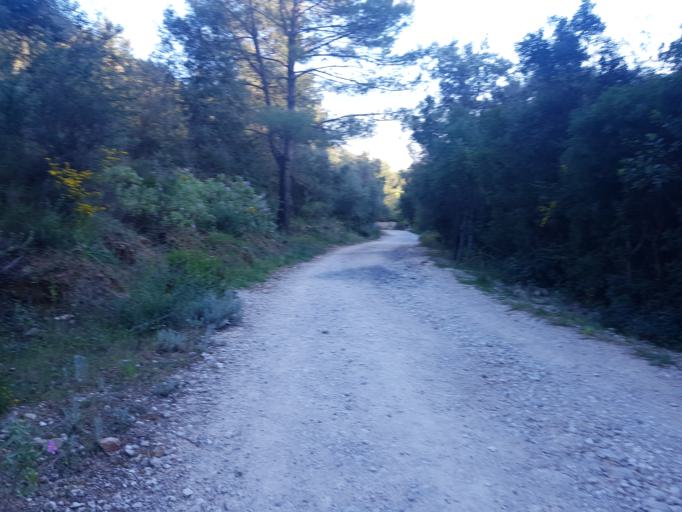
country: ES
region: Andalusia
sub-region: Provincia de Malaga
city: Marbella
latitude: 36.5352
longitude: -4.8846
